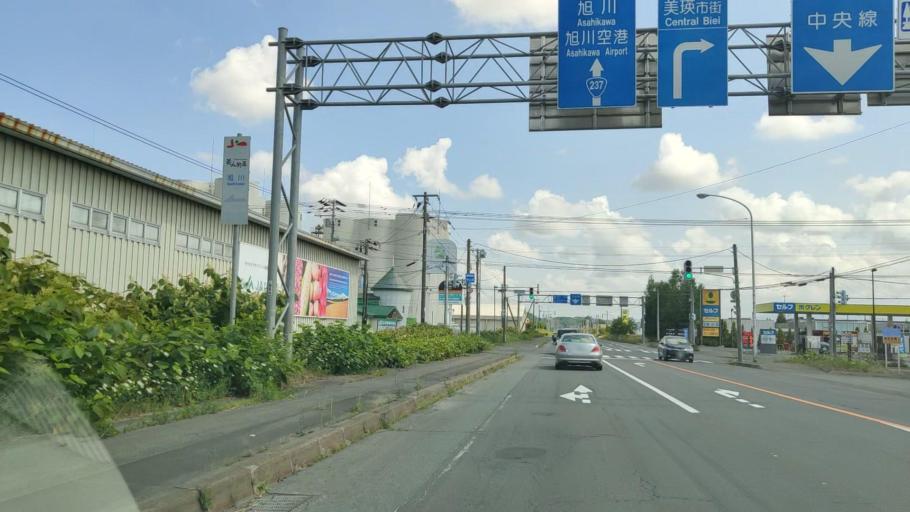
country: JP
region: Hokkaido
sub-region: Asahikawa-shi
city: Asahikawa
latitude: 43.5901
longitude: 142.4527
